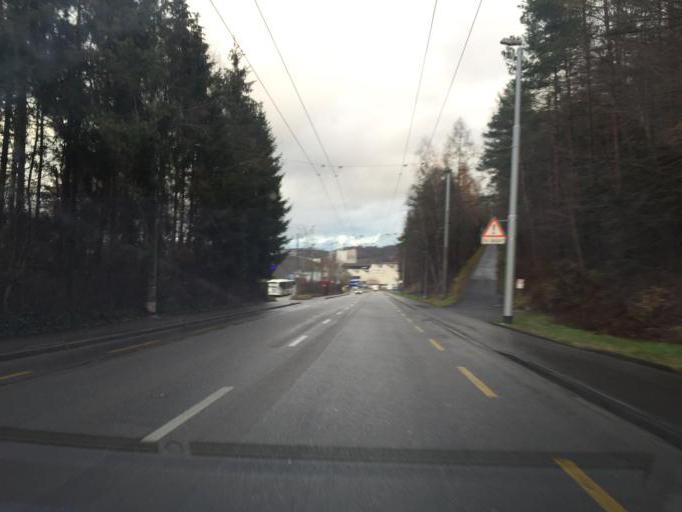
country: CH
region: Zurich
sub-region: Bezirk Andelfingen
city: Feuerthalen
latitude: 47.7118
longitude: 8.6543
